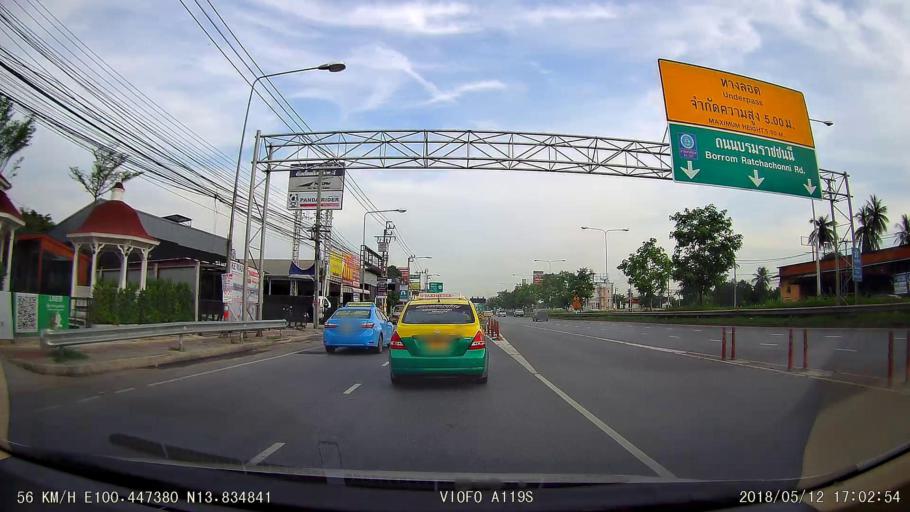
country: TH
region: Nonthaburi
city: Bang Kruai
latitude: 13.8344
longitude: 100.4475
